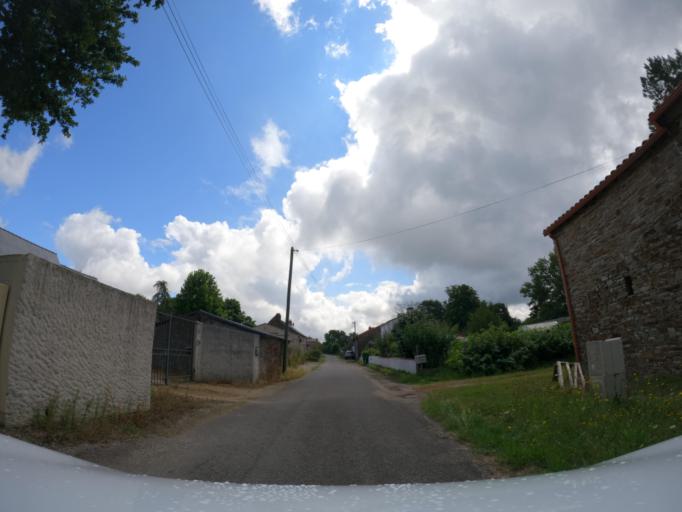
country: FR
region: Pays de la Loire
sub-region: Departement de la Loire-Atlantique
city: Saint-Mars-du-Desert
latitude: 47.3787
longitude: -1.4053
